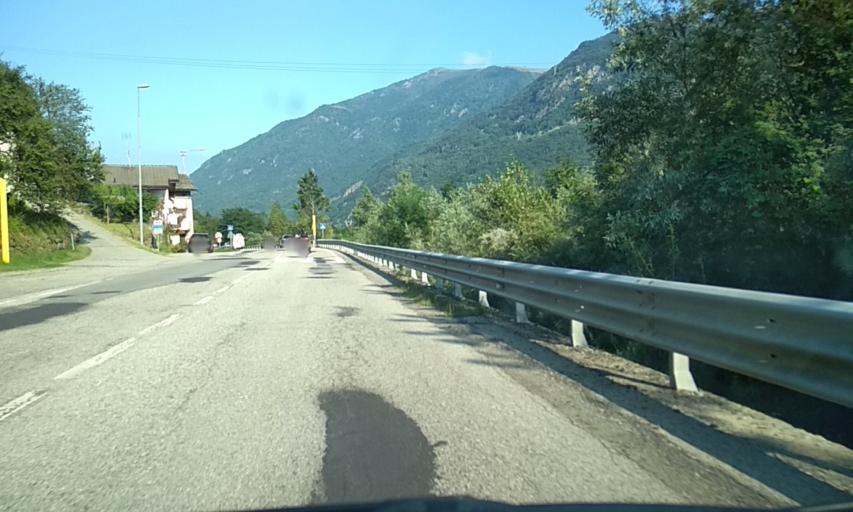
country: IT
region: Piedmont
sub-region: Provincia di Torino
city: Ribordone
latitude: 45.4068
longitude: 7.5024
